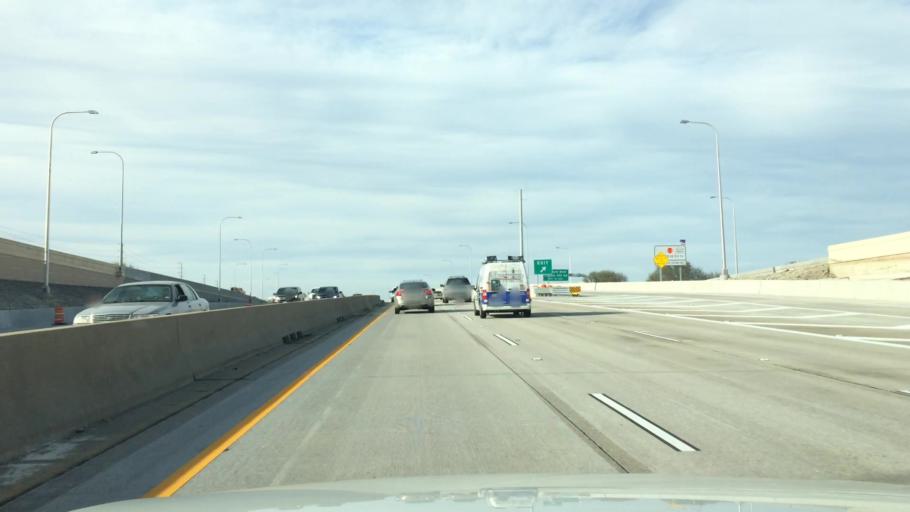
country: US
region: Texas
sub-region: Dallas County
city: Addison
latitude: 33.0176
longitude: -96.8292
